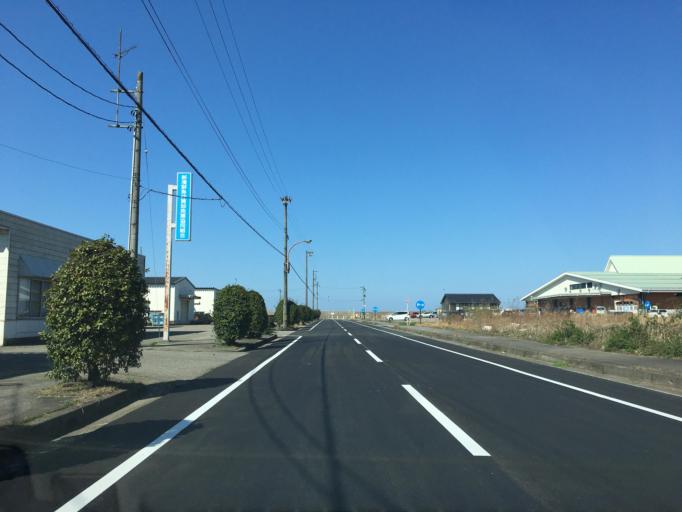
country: JP
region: Toyama
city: Nishishinminato
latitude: 36.7804
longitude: 137.0985
